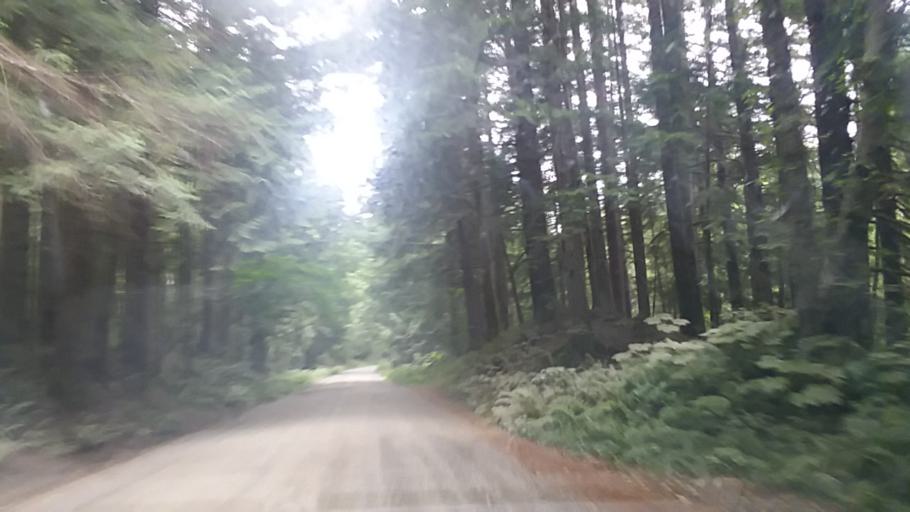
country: US
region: Washington
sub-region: King County
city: Tanner
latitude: 47.3954
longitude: -121.5536
